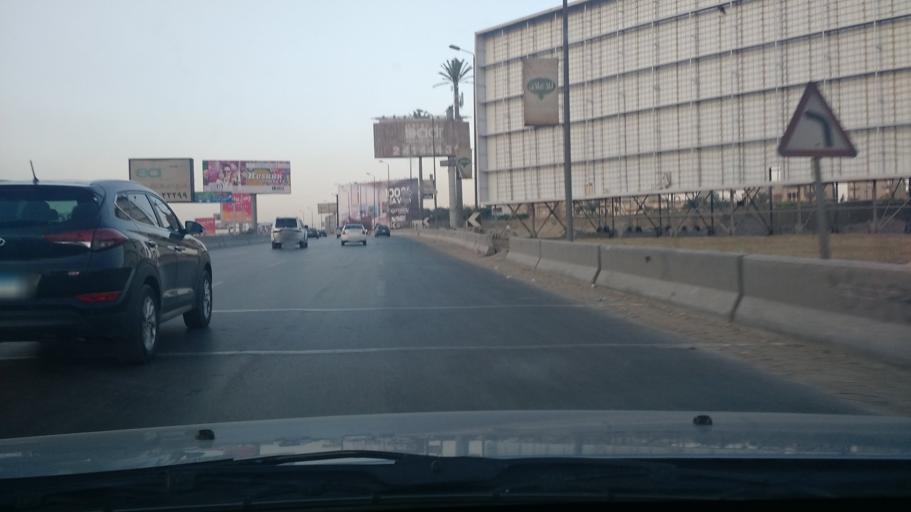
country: EG
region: Muhafazat al Qahirah
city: Cairo
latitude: 29.9957
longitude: 31.3905
